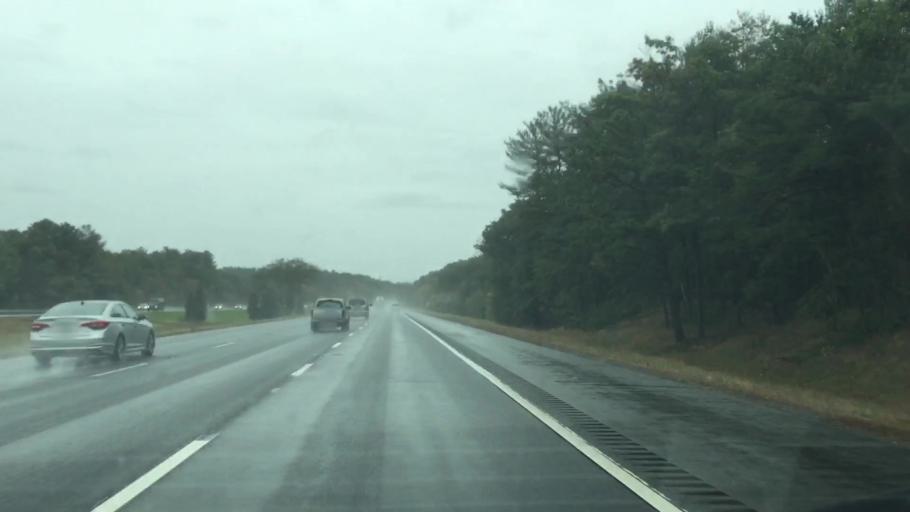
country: US
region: Massachusetts
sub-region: Essex County
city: Merrimac
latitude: 42.8089
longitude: -71.0294
